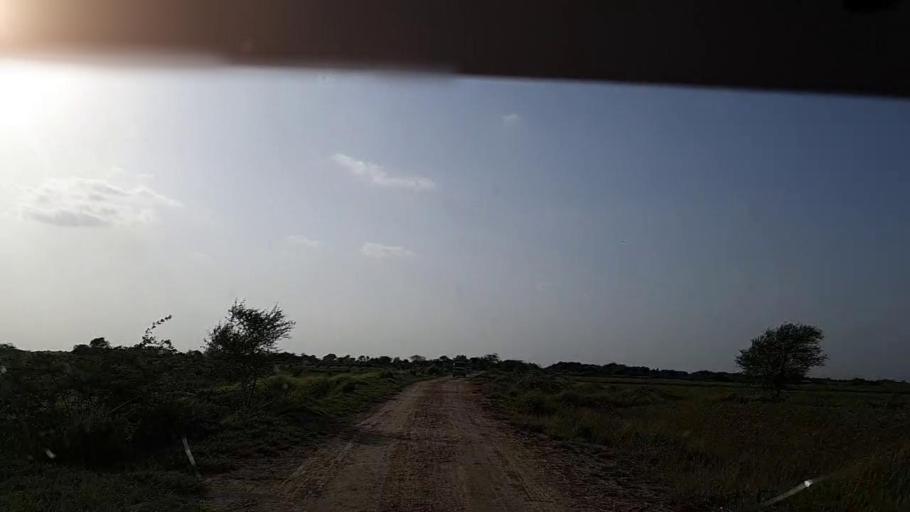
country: PK
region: Sindh
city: Badin
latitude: 24.5670
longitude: 68.8816
